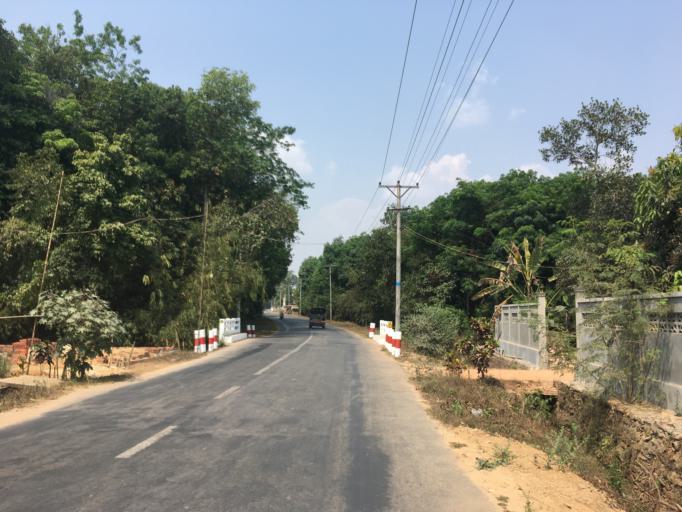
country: MM
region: Mon
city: Mawlamyine
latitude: 16.4496
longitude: 97.5227
